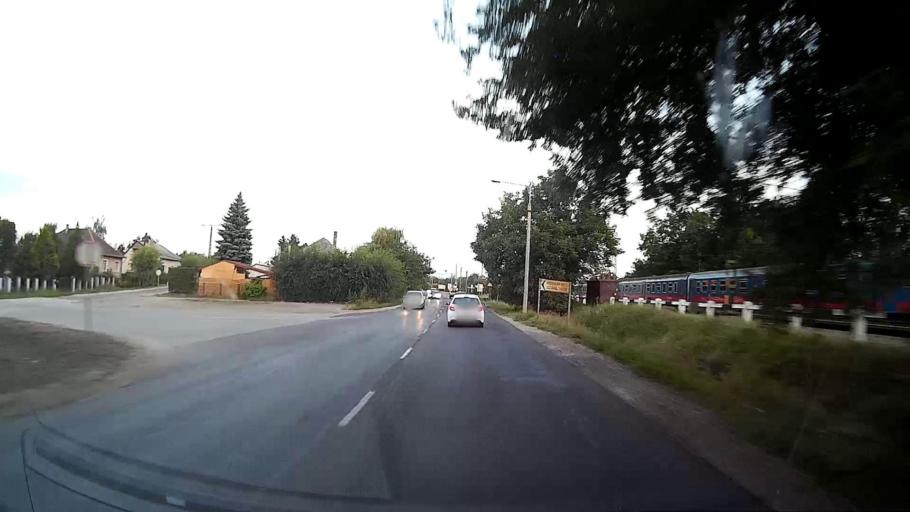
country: HU
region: Pest
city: Nyaregyhaza
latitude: 47.3094
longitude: 19.4991
